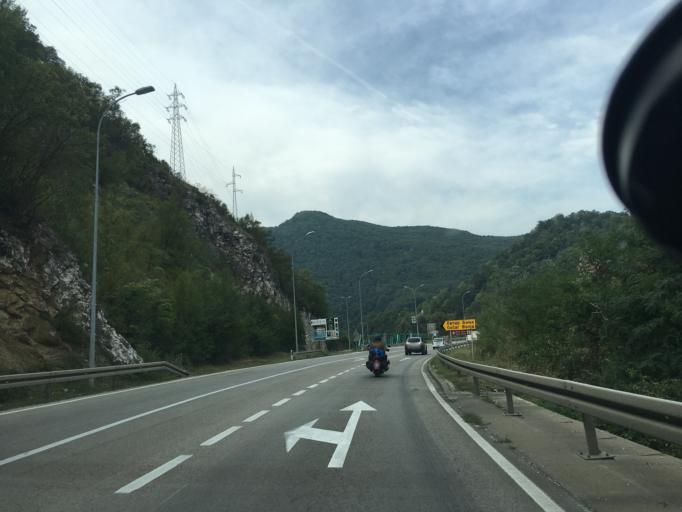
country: RS
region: Central Serbia
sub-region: Moravicki Okrug
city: Lucani
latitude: 43.9013
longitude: 20.1921
